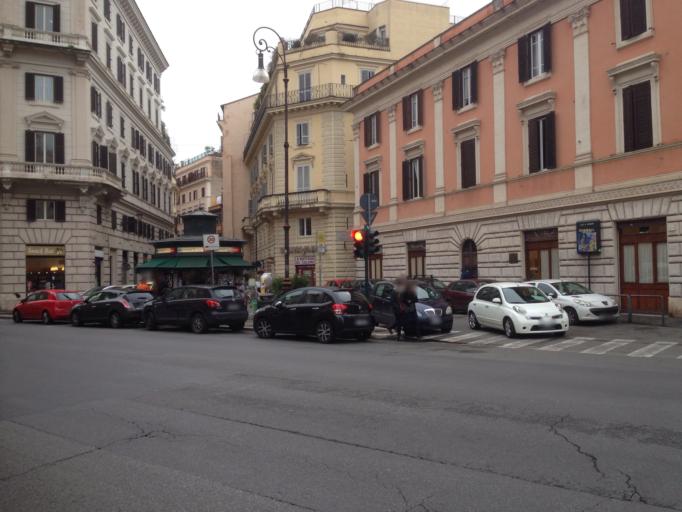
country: VA
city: Vatican City
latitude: 41.8996
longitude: 12.4665
